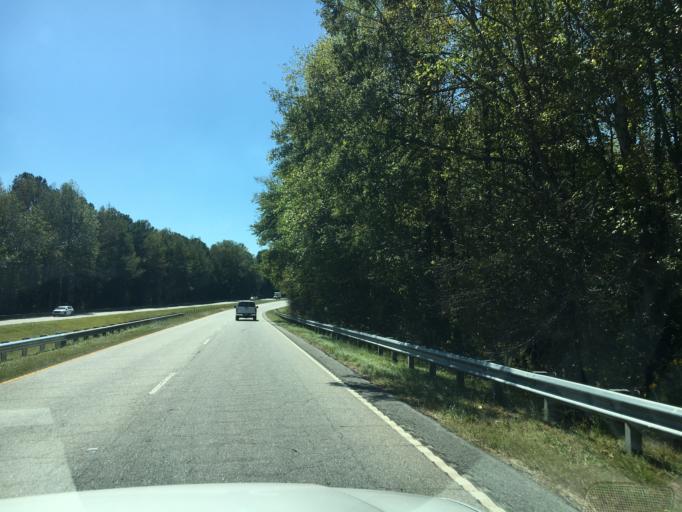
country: US
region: South Carolina
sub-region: Pickens County
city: Central
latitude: 34.7104
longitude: -82.7524
